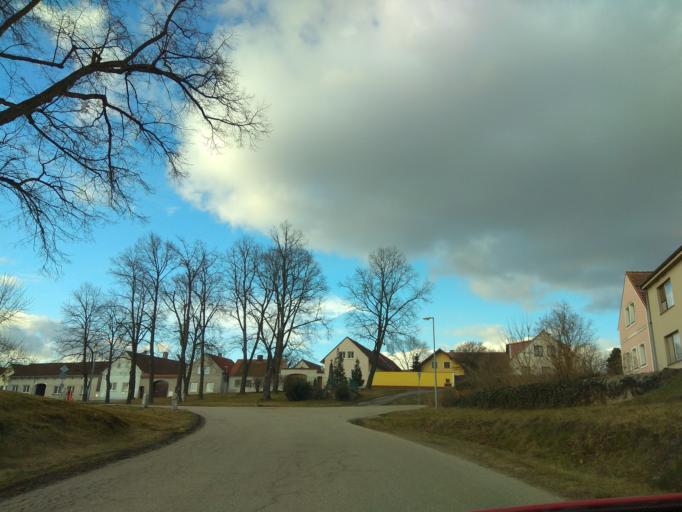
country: CZ
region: Jihocesky
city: Hrdejovice
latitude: 49.0389
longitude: 14.4758
